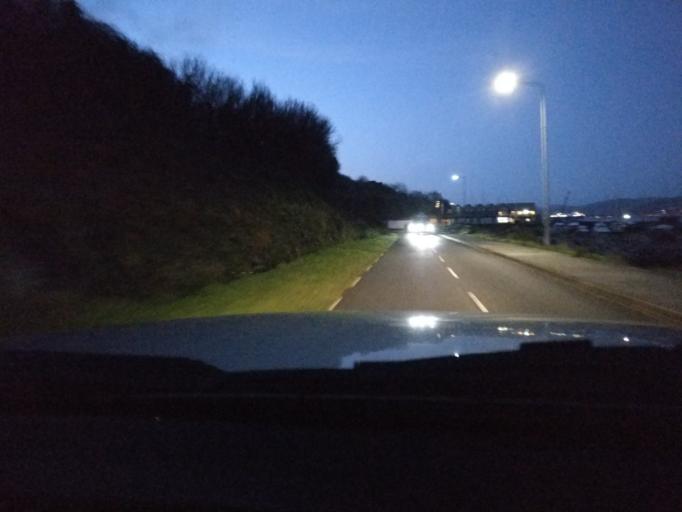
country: IE
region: Leinster
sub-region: Lu
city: Carlingford
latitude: 54.0495
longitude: -6.1911
